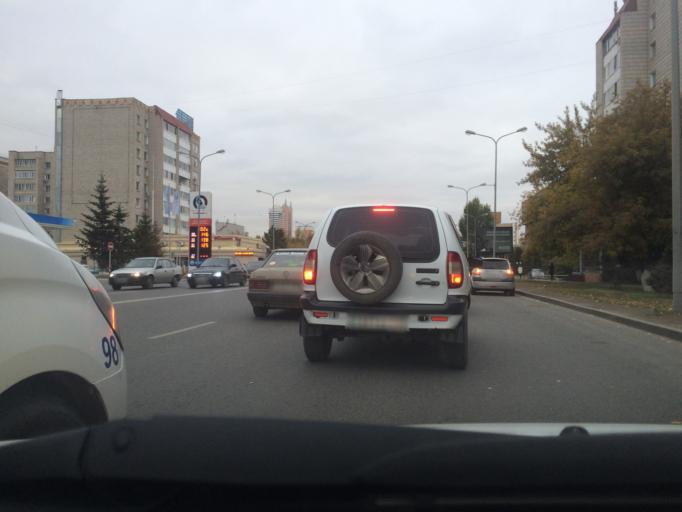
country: KZ
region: Astana Qalasy
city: Astana
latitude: 51.1730
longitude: 71.4251
